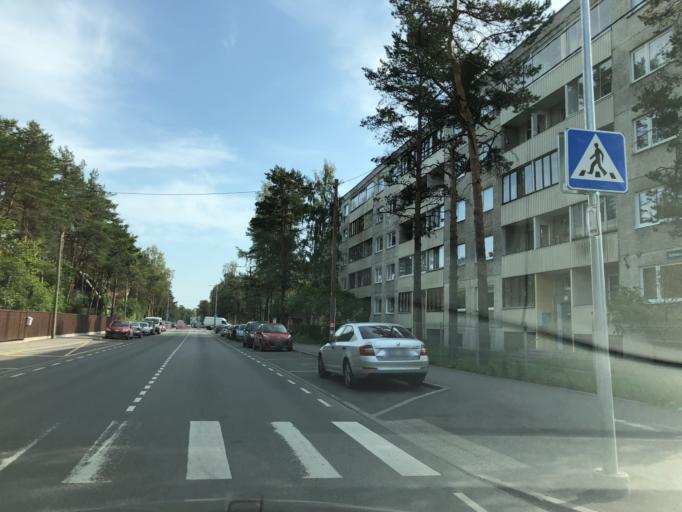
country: EE
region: Harju
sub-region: Tallinna linn
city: Tallinn
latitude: 59.3767
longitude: 24.7107
